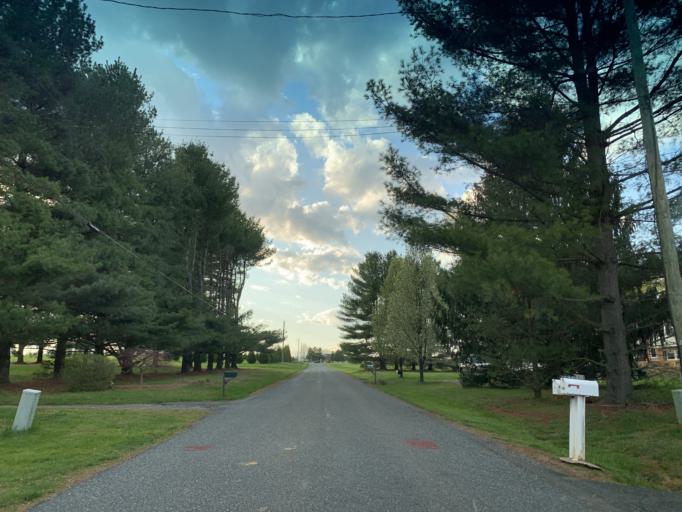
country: US
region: Maryland
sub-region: Harford County
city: South Bel Air
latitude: 39.5894
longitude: -76.3219
